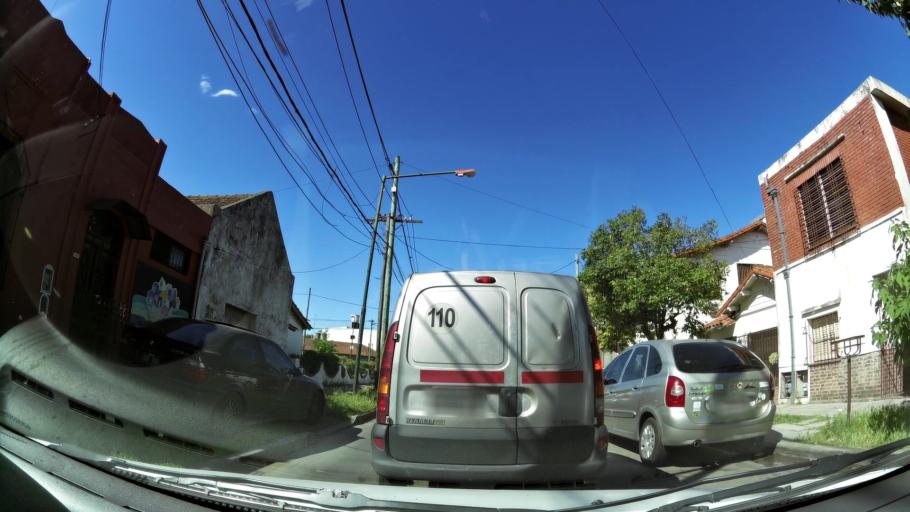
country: AR
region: Buenos Aires
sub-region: Partido de San Isidro
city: San Isidro
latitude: -34.5089
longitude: -58.5682
